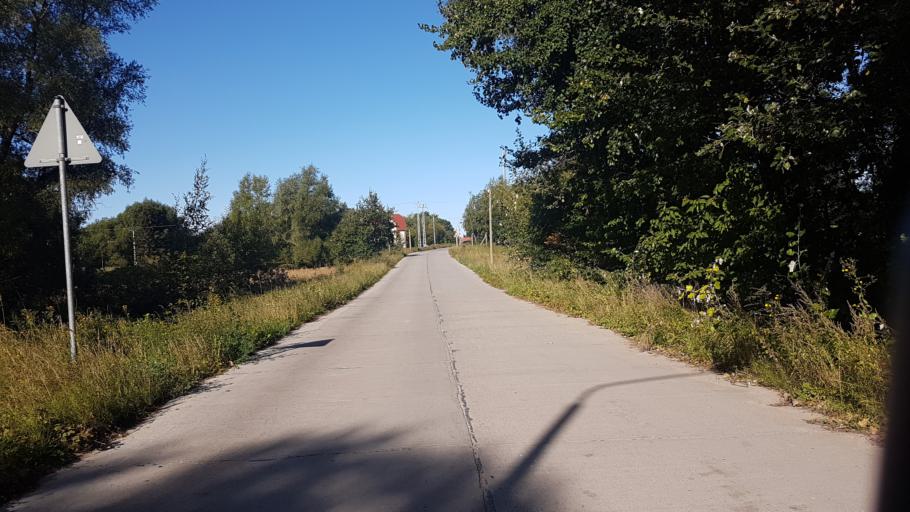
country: DE
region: Mecklenburg-Vorpommern
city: Sagard
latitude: 54.5024
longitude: 13.5331
